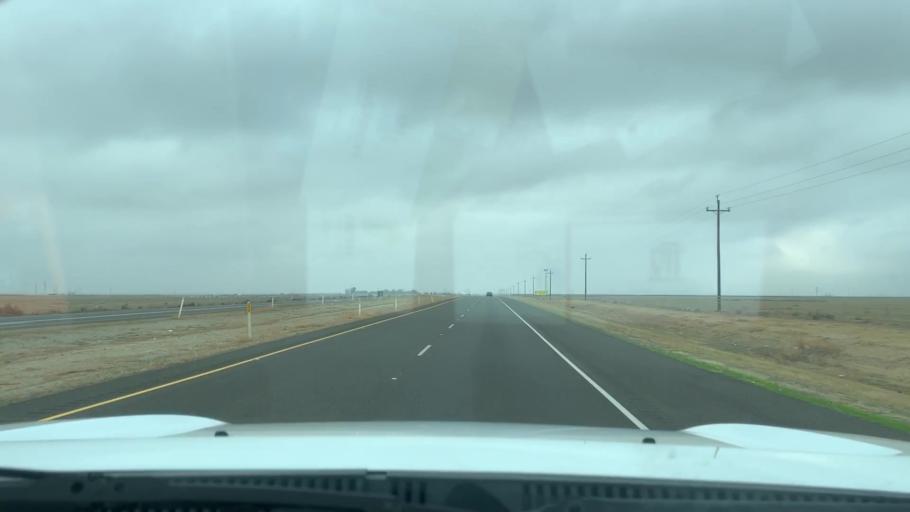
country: US
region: California
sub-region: Kern County
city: Lost Hills
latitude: 35.6155
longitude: -119.8350
